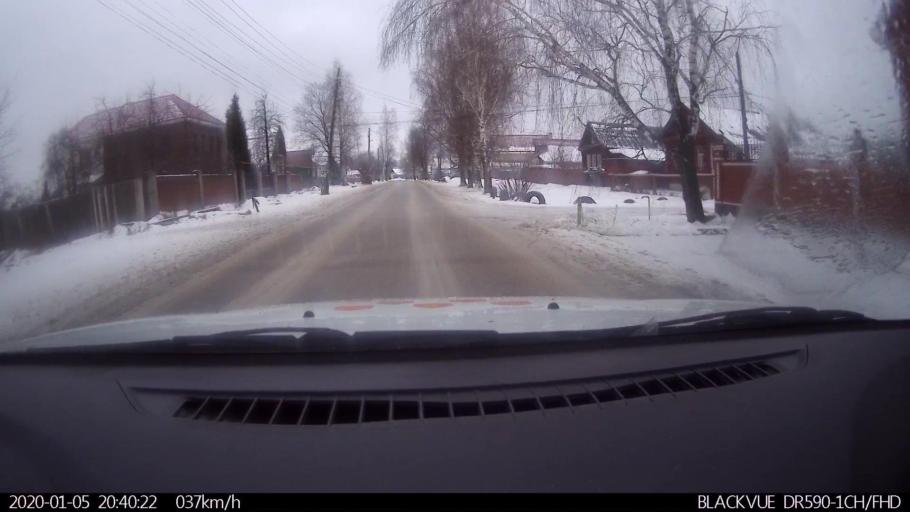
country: RU
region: Nizjnij Novgorod
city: Lukino
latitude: 56.4101
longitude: 43.7290
